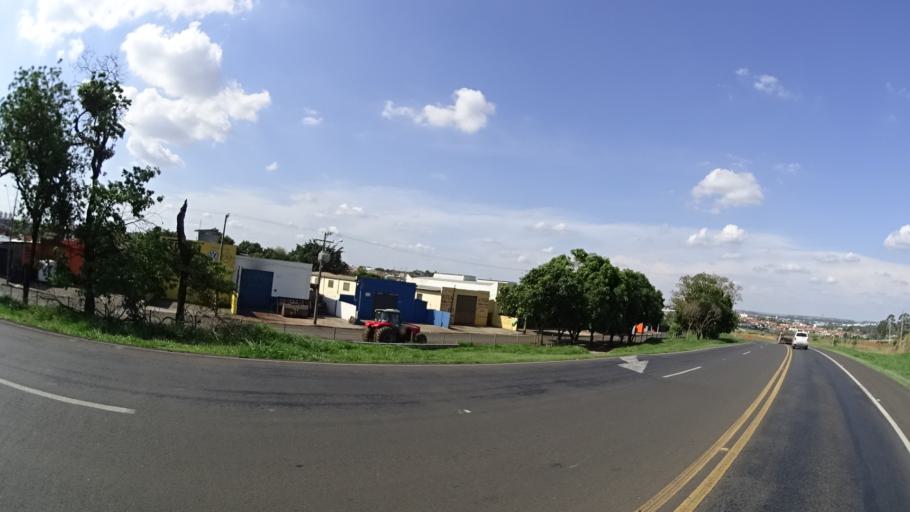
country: BR
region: Sao Paulo
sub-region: Sao Jose Do Rio Preto
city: Sao Jose do Rio Preto
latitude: -20.8502
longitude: -49.3793
